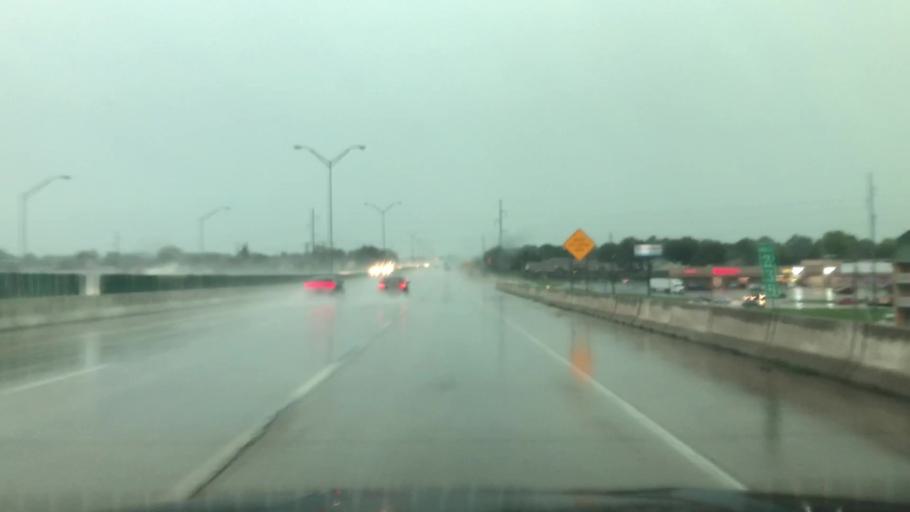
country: US
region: Oklahoma
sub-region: Tulsa County
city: Broken Arrow
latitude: 36.1472
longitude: -95.8492
